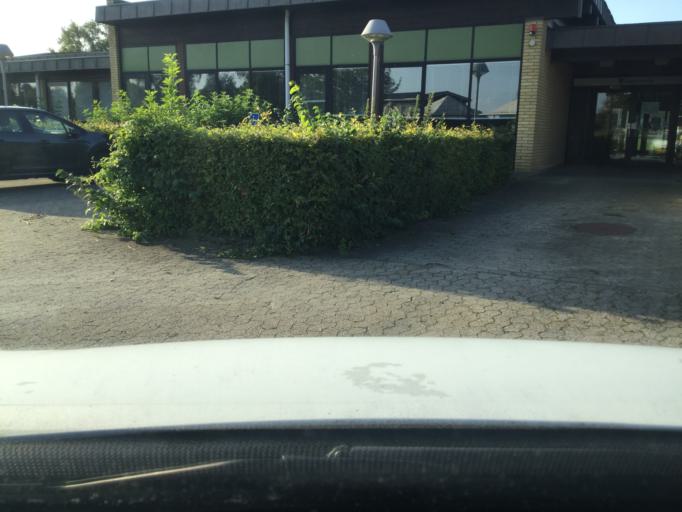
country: DK
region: Zealand
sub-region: Lolland Kommune
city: Rodby
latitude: 54.6971
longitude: 11.3889
